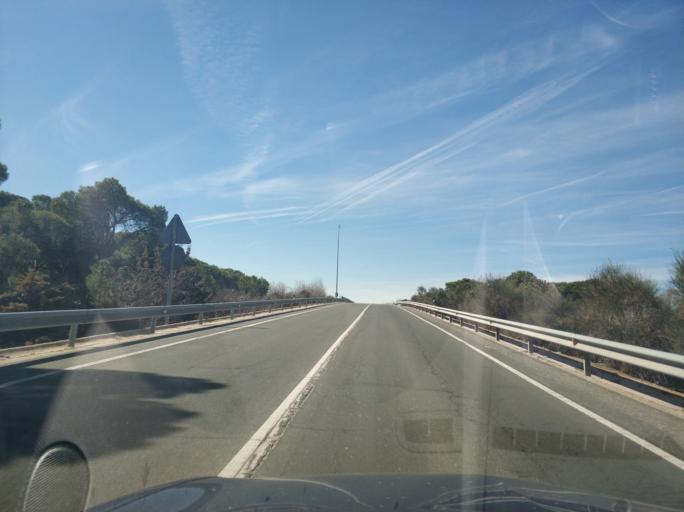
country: ES
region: Castille and Leon
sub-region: Provincia de Valladolid
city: Tordesillas
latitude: 41.4901
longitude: -5.0220
